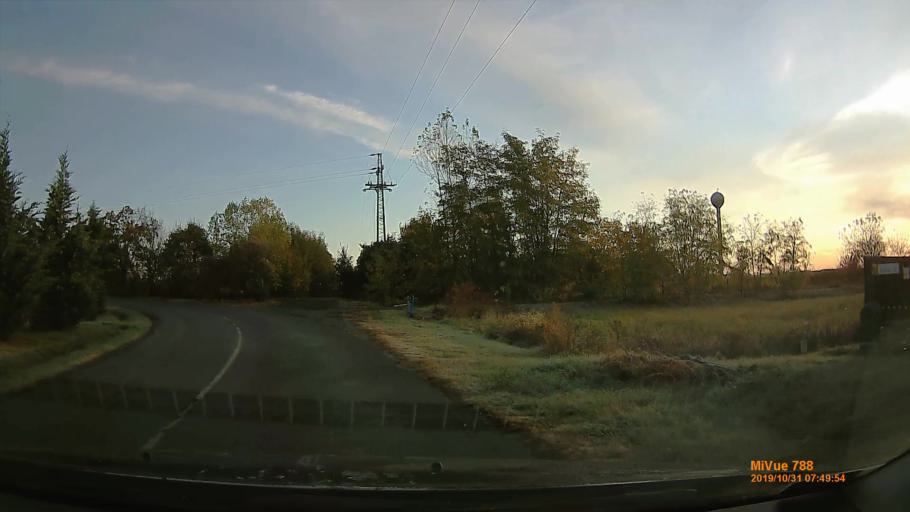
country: HU
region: Pest
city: Pilis
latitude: 47.2992
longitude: 19.5613
